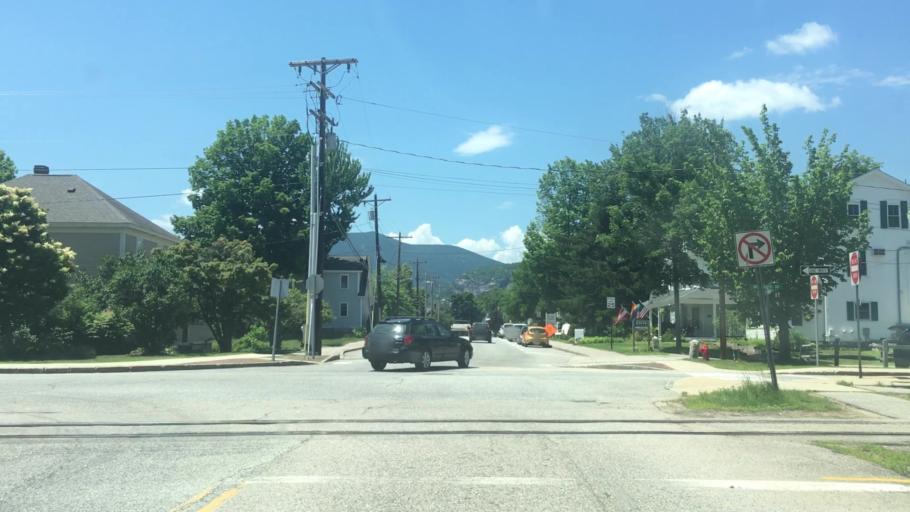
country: US
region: New Hampshire
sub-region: Carroll County
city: North Conway
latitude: 44.0533
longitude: -71.1240
